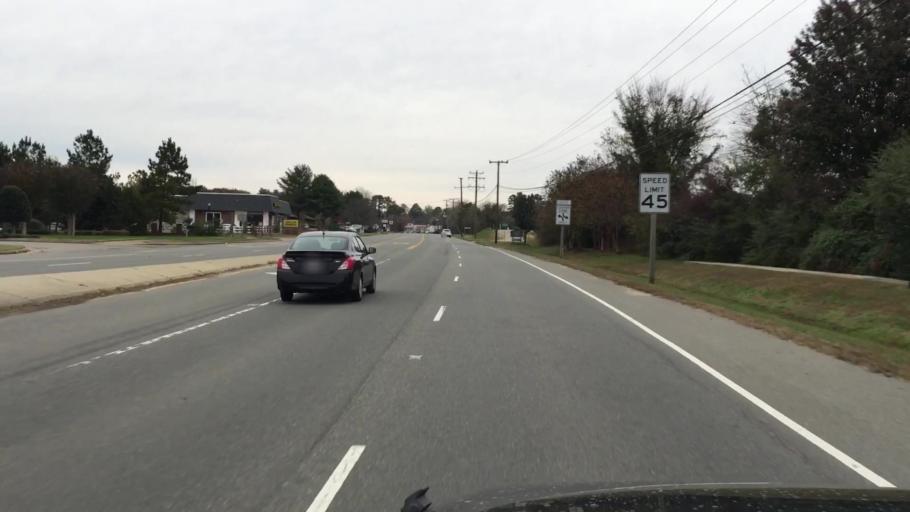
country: US
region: Virginia
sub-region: James City County
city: Williamsburg
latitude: 37.3587
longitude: -76.7645
